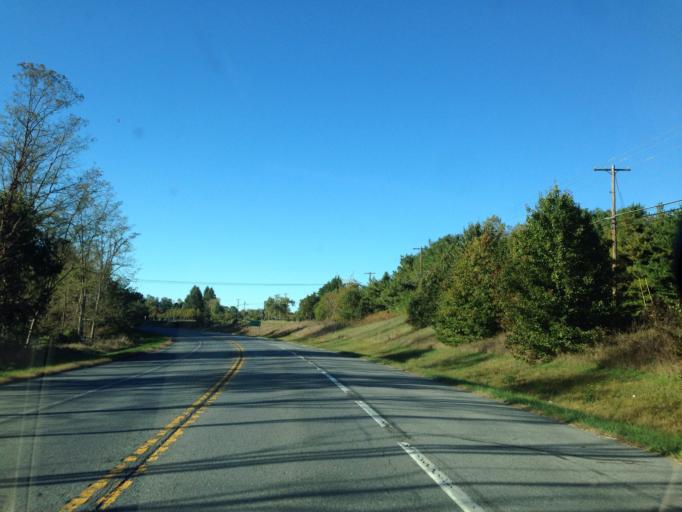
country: US
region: Maryland
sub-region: Carroll County
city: Mount Airy
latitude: 39.3950
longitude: -77.1395
